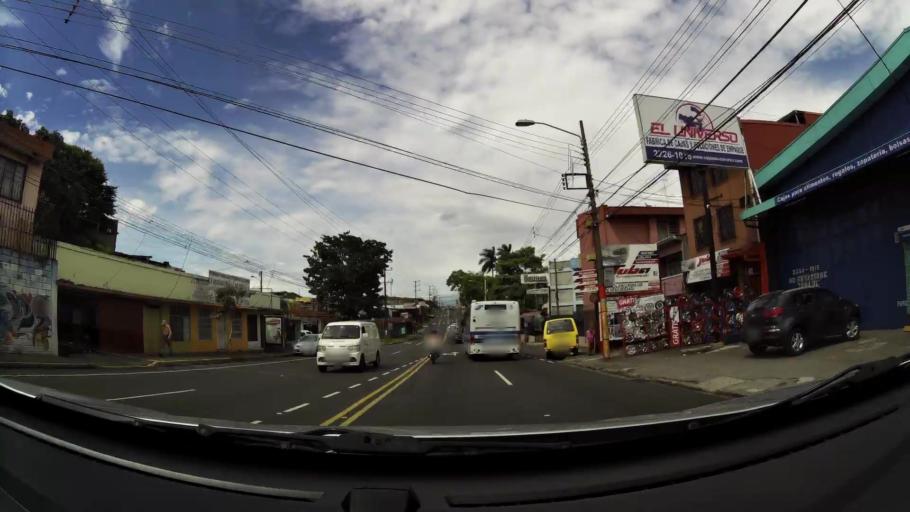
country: CR
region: San Jose
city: San Jose
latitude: 9.9195
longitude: -84.0714
